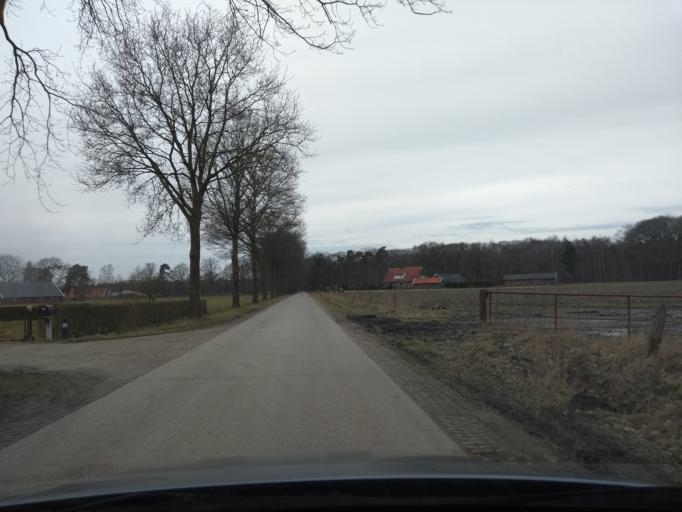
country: NL
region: Overijssel
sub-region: Gemeente Almelo
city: Almelo
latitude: 52.3588
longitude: 6.7244
